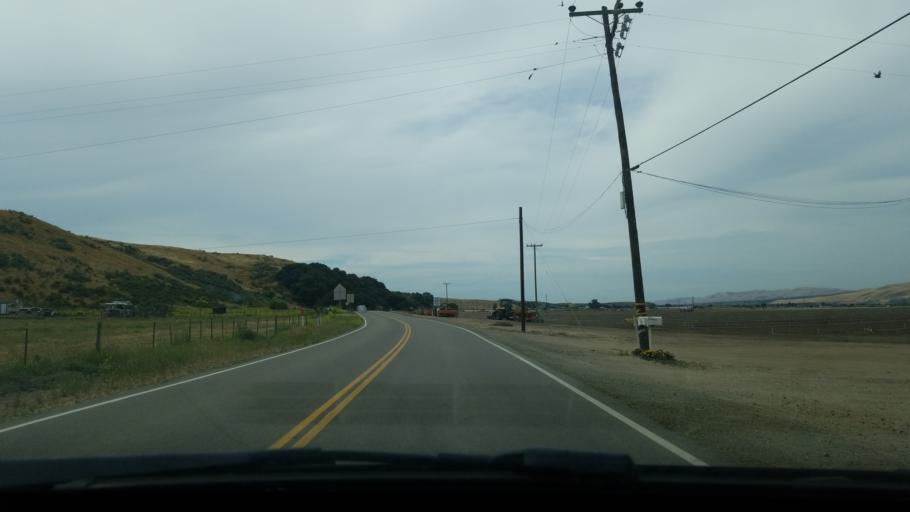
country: US
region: California
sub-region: Santa Barbara County
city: Los Alamos
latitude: 34.8682
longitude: -120.2976
